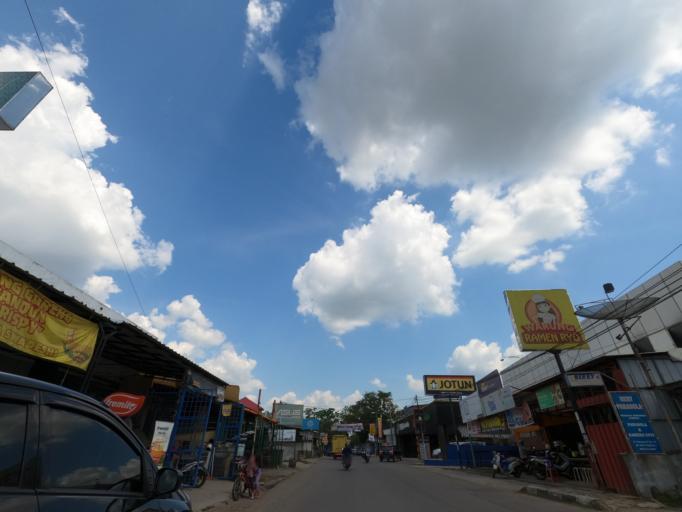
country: ID
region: West Java
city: Pamanukan
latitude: -6.5608
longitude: 107.7650
